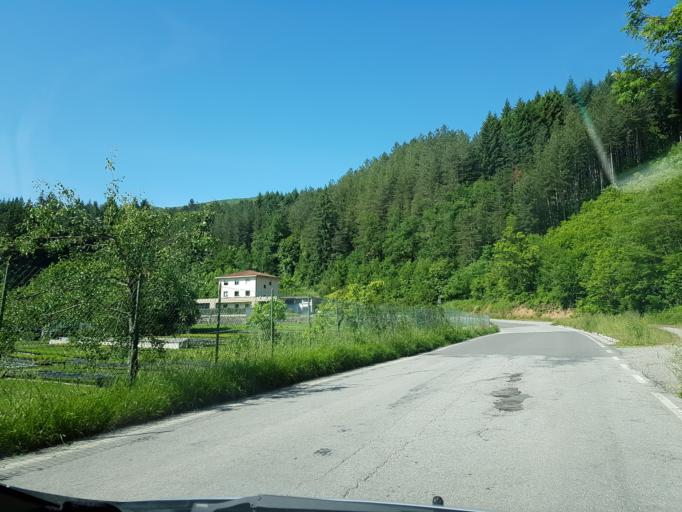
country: IT
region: Tuscany
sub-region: Provincia di Lucca
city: Camporgiano
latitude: 44.1666
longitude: 10.3282
